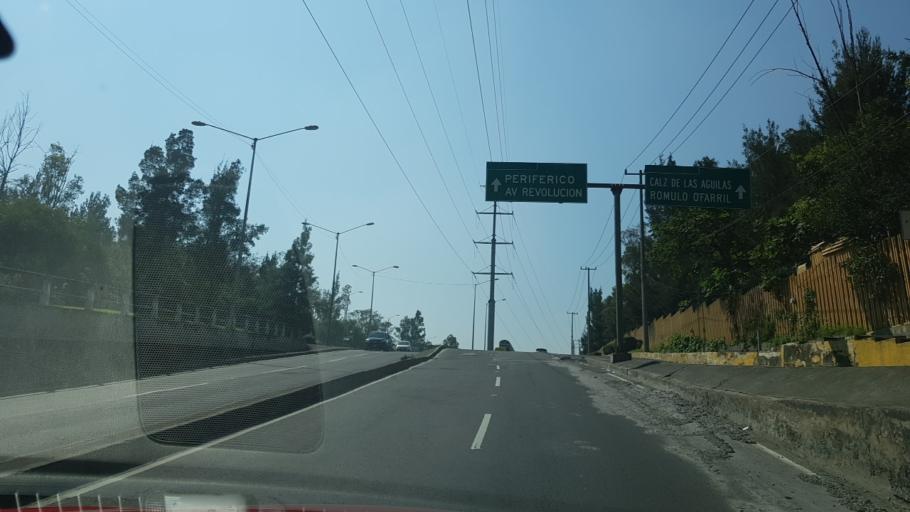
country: MX
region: Mexico City
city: Alvaro Obregon
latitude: 19.3586
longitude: -99.2067
